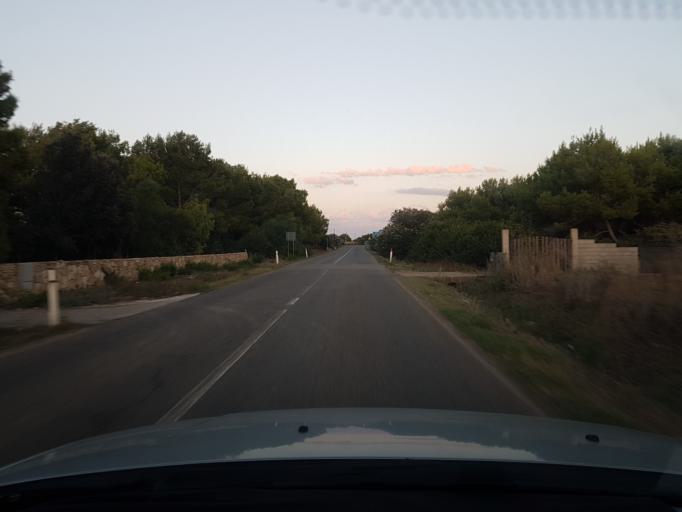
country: IT
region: Sardinia
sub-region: Provincia di Oristano
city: Riola Sardo
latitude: 40.0277
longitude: 8.4260
